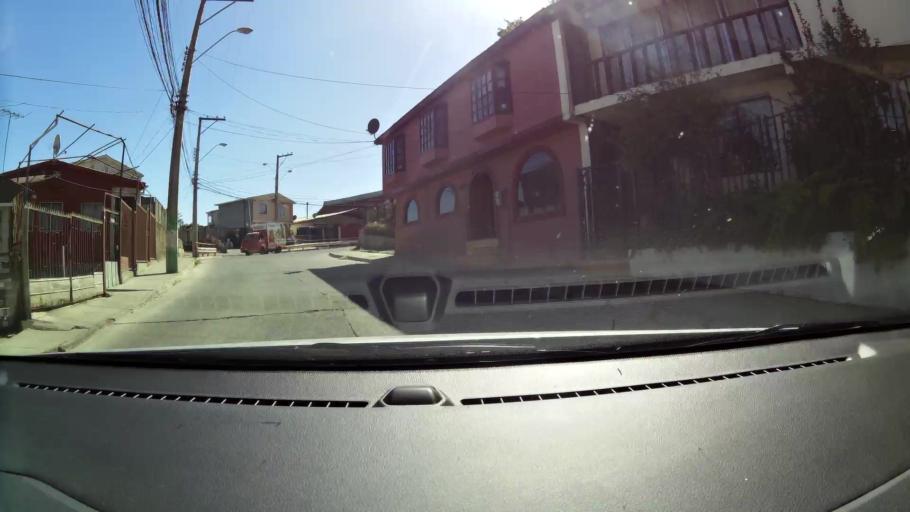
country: CL
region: Valparaiso
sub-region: Provincia de Valparaiso
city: Valparaiso
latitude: -33.0646
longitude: -71.5917
